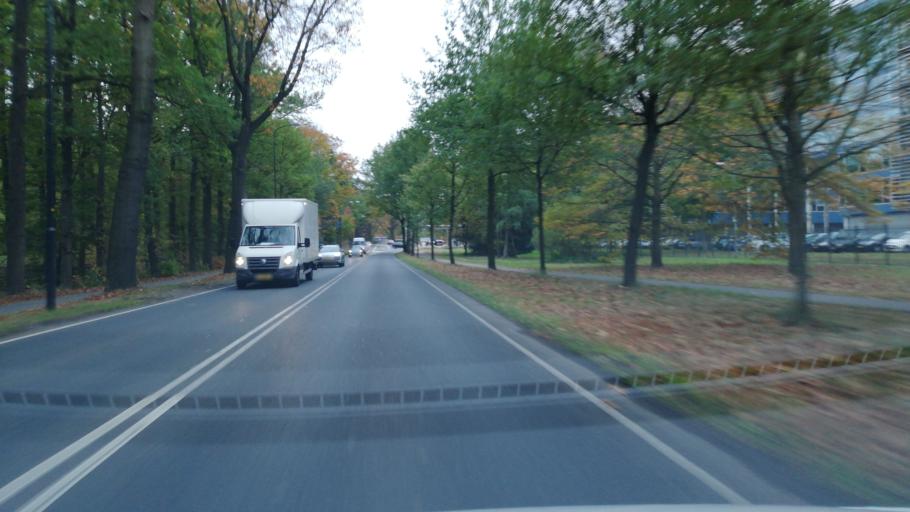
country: NL
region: Gelderland
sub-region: Gemeente Apeldoorn
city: Beekbergen
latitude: 52.1773
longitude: 5.9621
